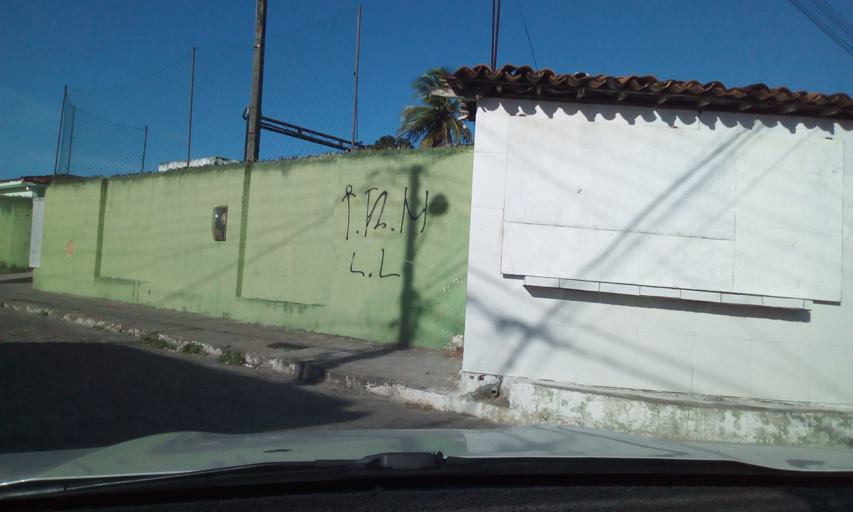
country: BR
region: Paraiba
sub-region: Bayeux
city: Bayeux
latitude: -7.1274
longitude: -34.9163
